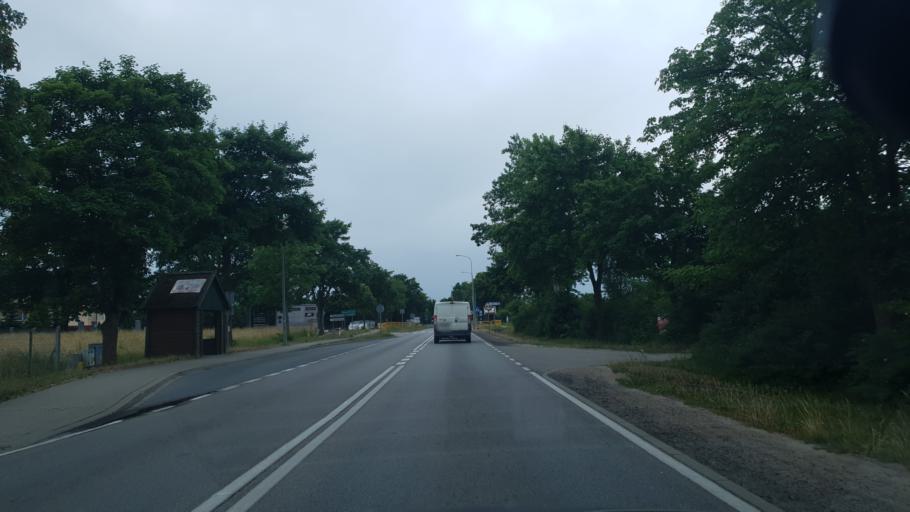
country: PL
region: Pomeranian Voivodeship
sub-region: Powiat kartuski
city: Banino
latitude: 54.4114
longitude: 18.3711
